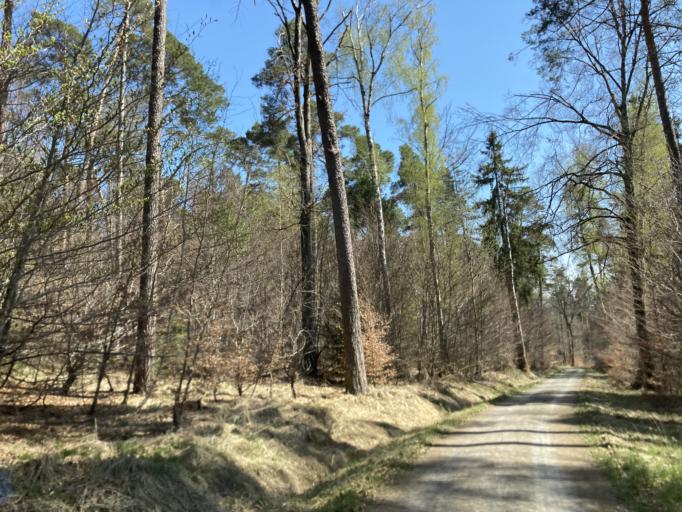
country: DE
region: Baden-Wuerttemberg
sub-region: Tuebingen Region
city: Tuebingen
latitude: 48.5713
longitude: 9.0155
